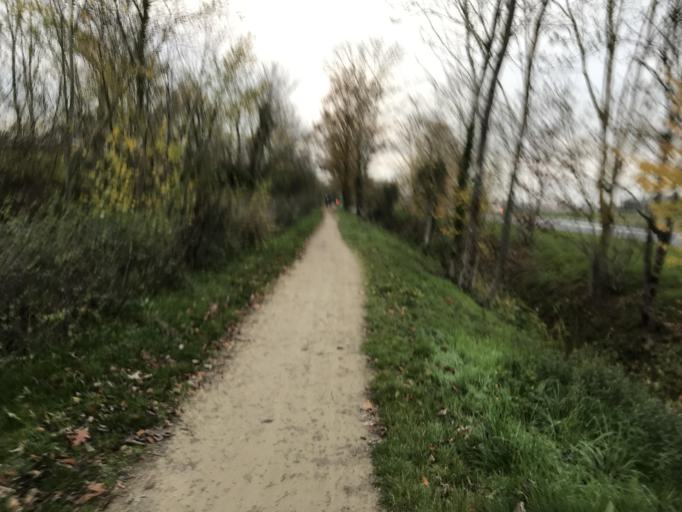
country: FR
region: Ile-de-France
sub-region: Departement de l'Essonne
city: Villiers-le-Bacle
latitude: 48.7322
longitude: 2.1055
